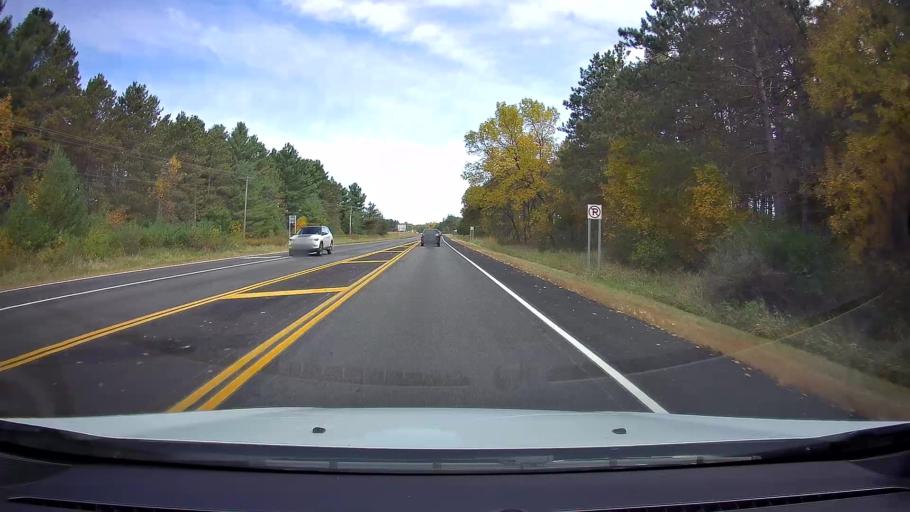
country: US
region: Minnesota
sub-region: Washington County
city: Scandia
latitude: 45.2257
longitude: -92.7635
